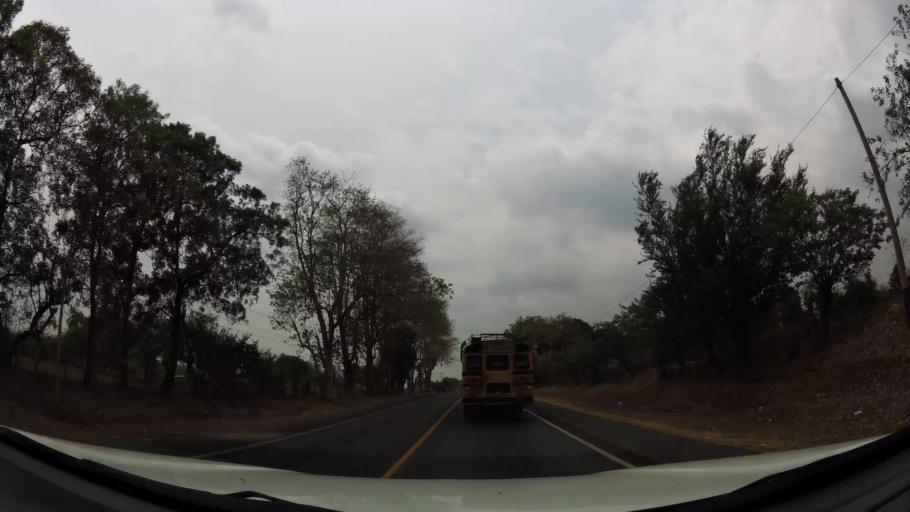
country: NI
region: Leon
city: Telica
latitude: 12.5188
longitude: -86.8662
